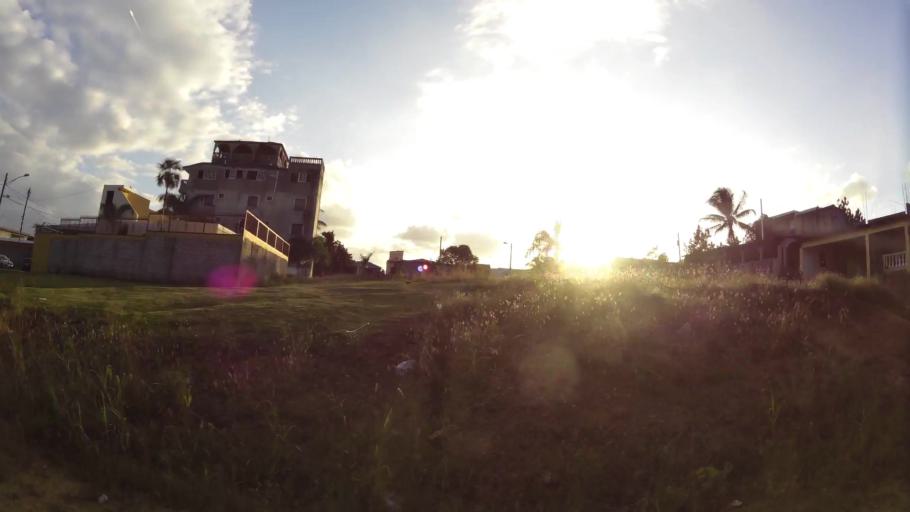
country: DO
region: Nacional
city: La Agustina
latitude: 18.5511
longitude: -69.9191
